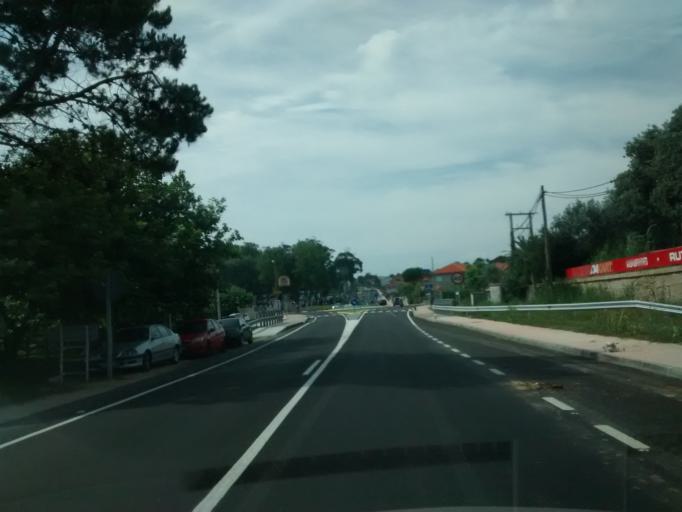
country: ES
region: Galicia
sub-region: Provincia de Pontevedra
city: Sanxenxo
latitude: 42.4158
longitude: -8.8674
